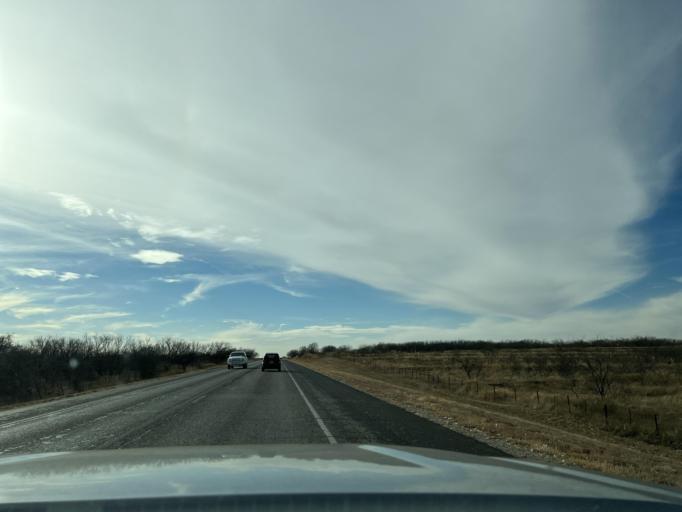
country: US
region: Texas
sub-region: Fisher County
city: Roby
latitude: 32.7547
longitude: -100.3344
